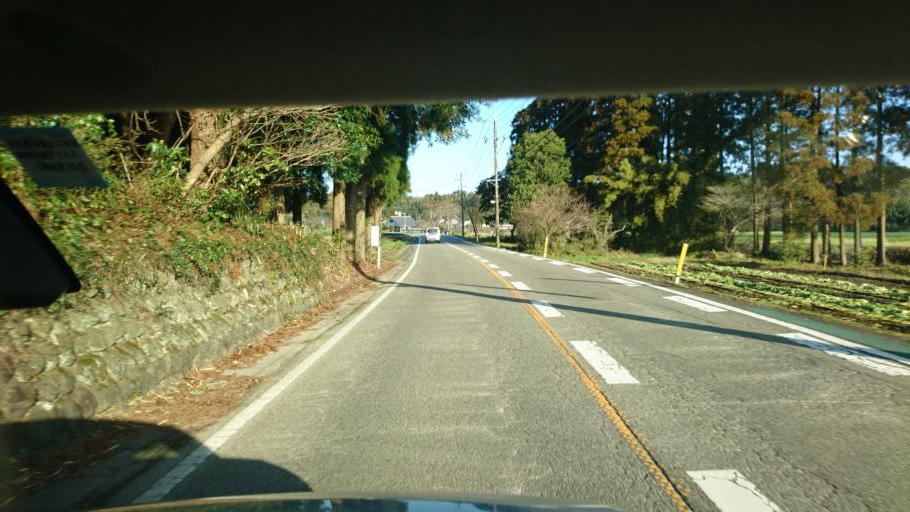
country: JP
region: Miyazaki
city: Miyazaki-shi
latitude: 31.8562
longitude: 131.3731
